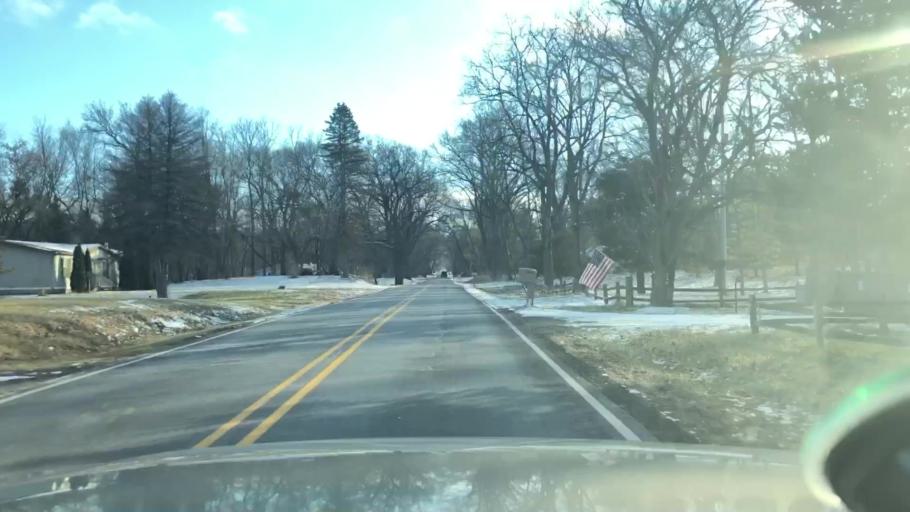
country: US
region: Michigan
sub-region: Jackson County
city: Vandercook Lake
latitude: 42.1536
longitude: -84.4521
